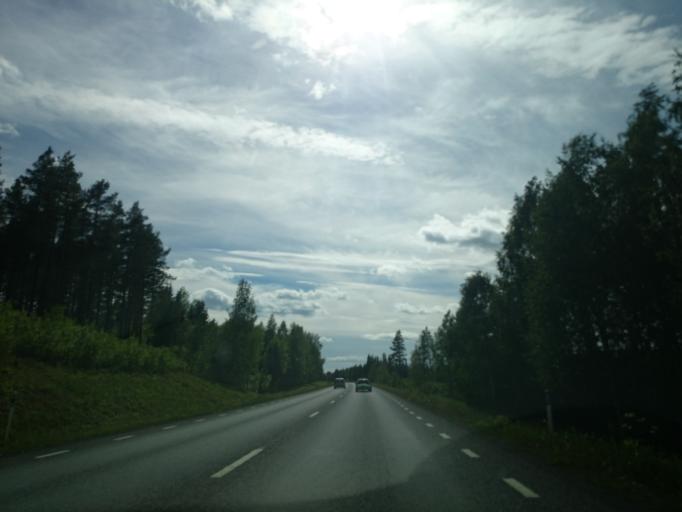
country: SE
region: Jaemtland
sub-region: Krokoms Kommun
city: Valla
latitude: 63.3220
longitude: 13.9438
